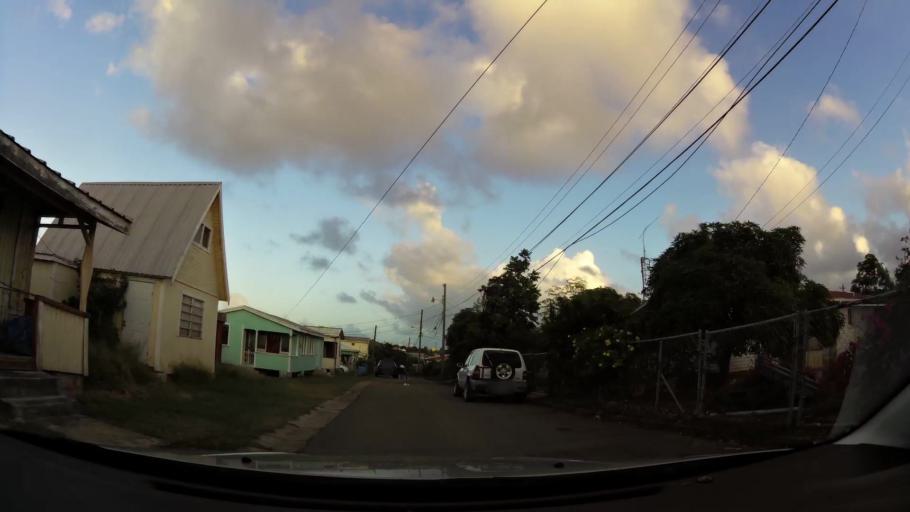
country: AG
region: Saint John
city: Saint John's
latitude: 17.1359
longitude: -61.8438
